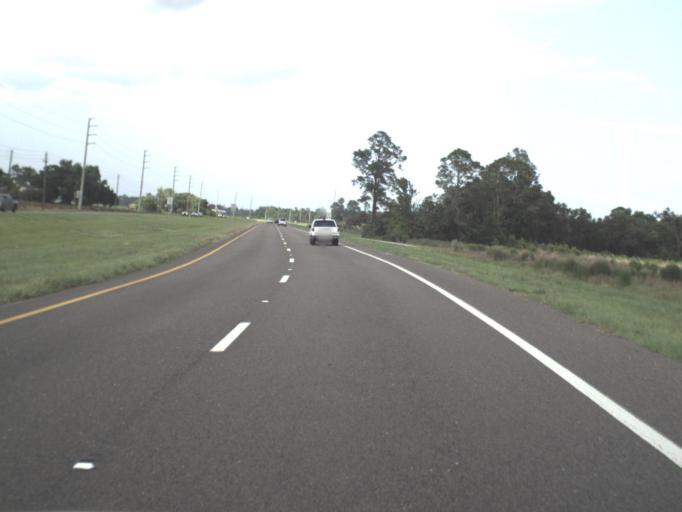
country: US
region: Florida
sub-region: Putnam County
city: East Palatka
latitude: 29.7455
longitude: -81.4709
